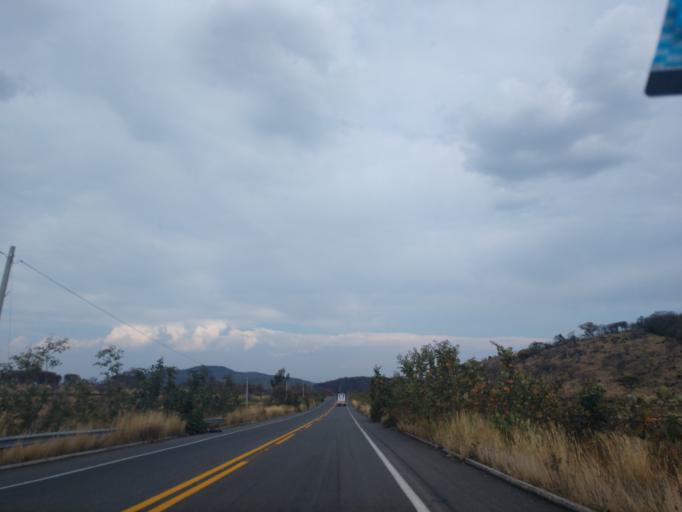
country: MX
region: Jalisco
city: La Manzanilla de la Paz
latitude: 20.1197
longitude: -103.1648
